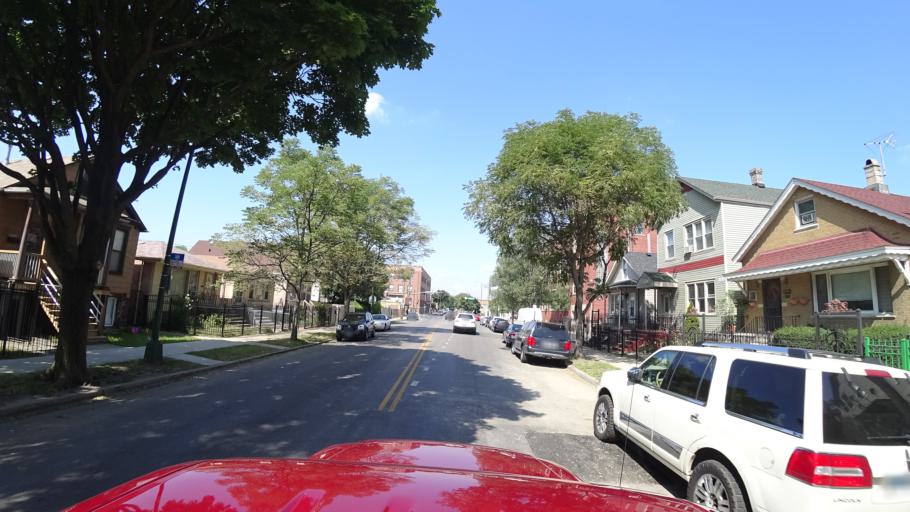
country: US
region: Illinois
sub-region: Cook County
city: Chicago
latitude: 41.8228
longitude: -87.6934
